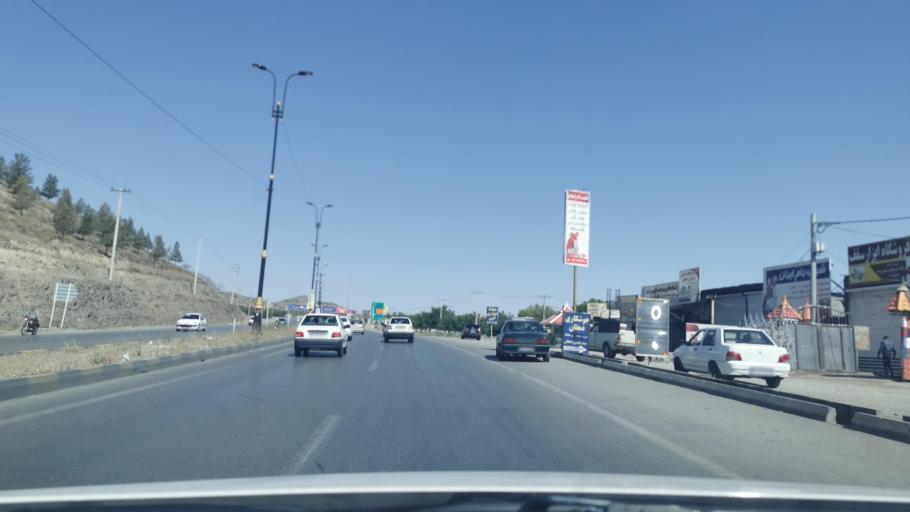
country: IR
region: Razavi Khorasan
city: Torqabeh
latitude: 36.4022
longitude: 59.3868
